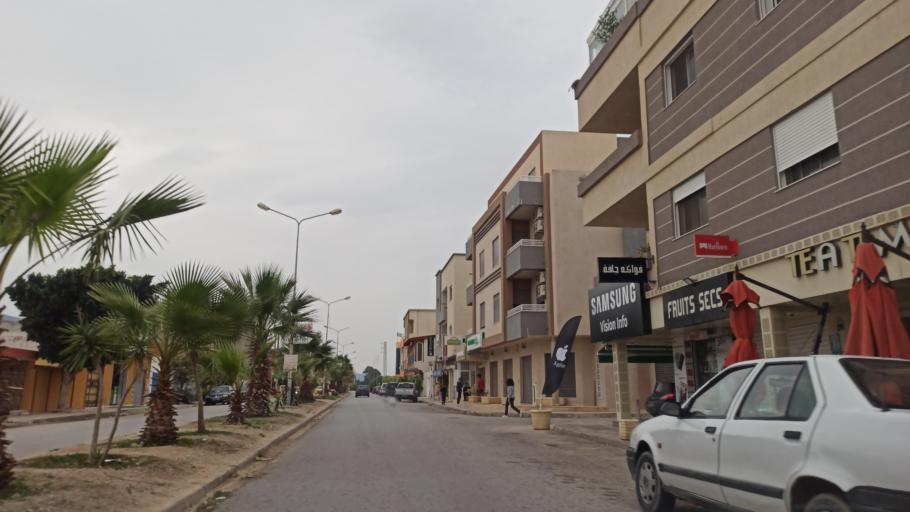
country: TN
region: Tunis
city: Hammam-Lif
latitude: 36.7089
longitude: 10.4142
